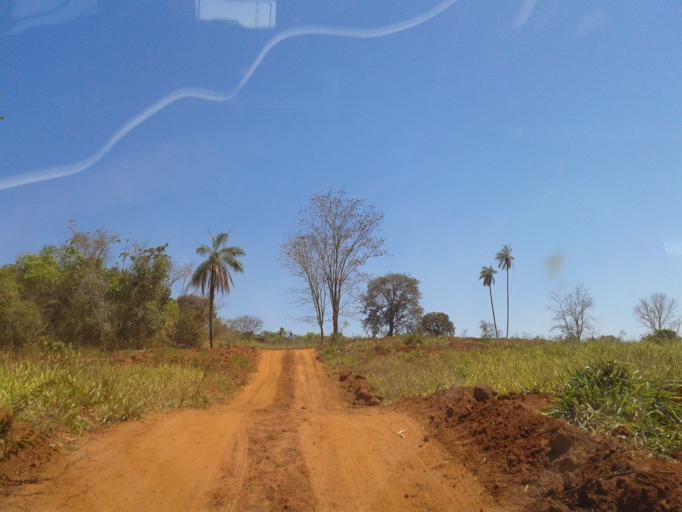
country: BR
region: Minas Gerais
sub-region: Ituiutaba
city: Ituiutaba
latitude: -19.0865
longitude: -49.2613
